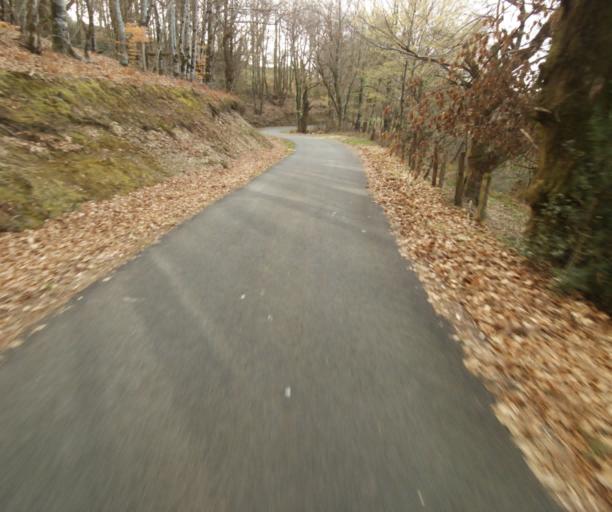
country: FR
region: Limousin
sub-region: Departement de la Correze
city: Chamboulive
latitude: 45.4335
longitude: 1.7895
